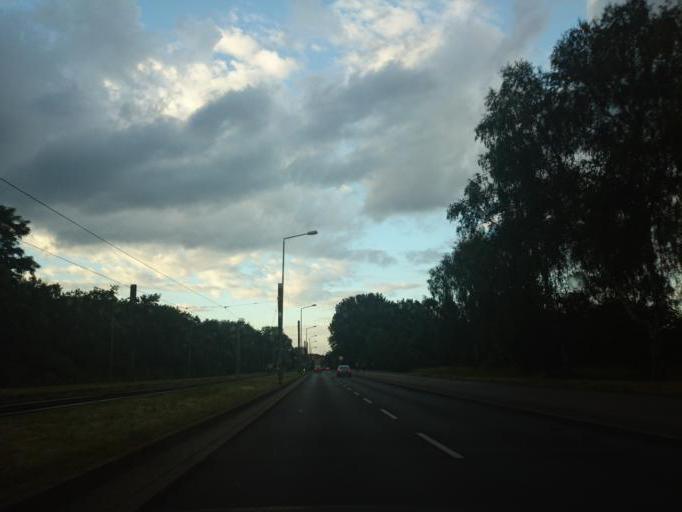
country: DE
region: Berlin
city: Oberschoneweide
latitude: 52.4729
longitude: 13.5191
